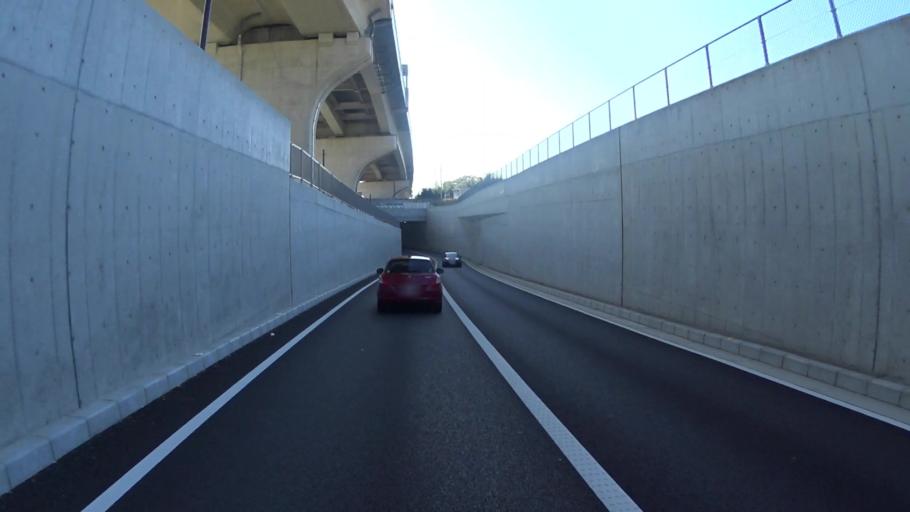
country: JP
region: Kyoto
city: Yawata
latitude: 34.9101
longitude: 135.6907
